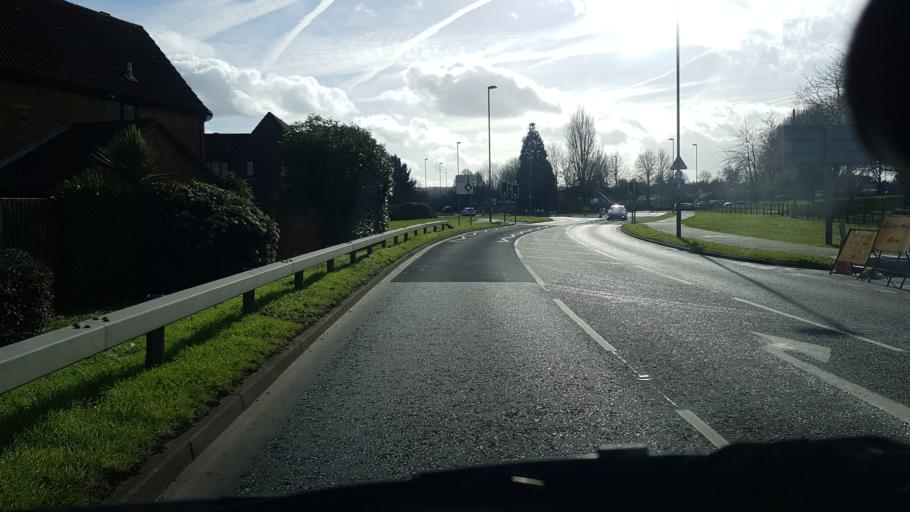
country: GB
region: England
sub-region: Surrey
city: Send
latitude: 51.2630
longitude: -0.5482
